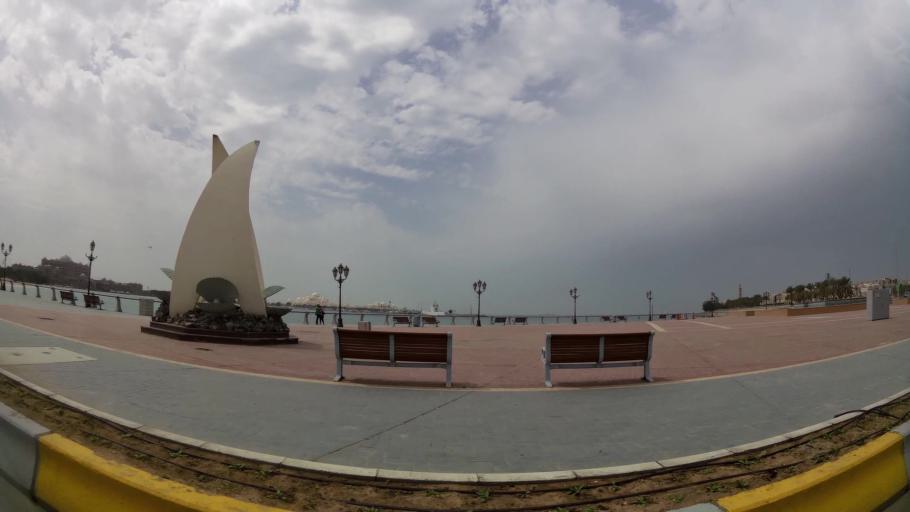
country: AE
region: Abu Dhabi
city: Abu Dhabi
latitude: 24.4704
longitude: 54.3220
